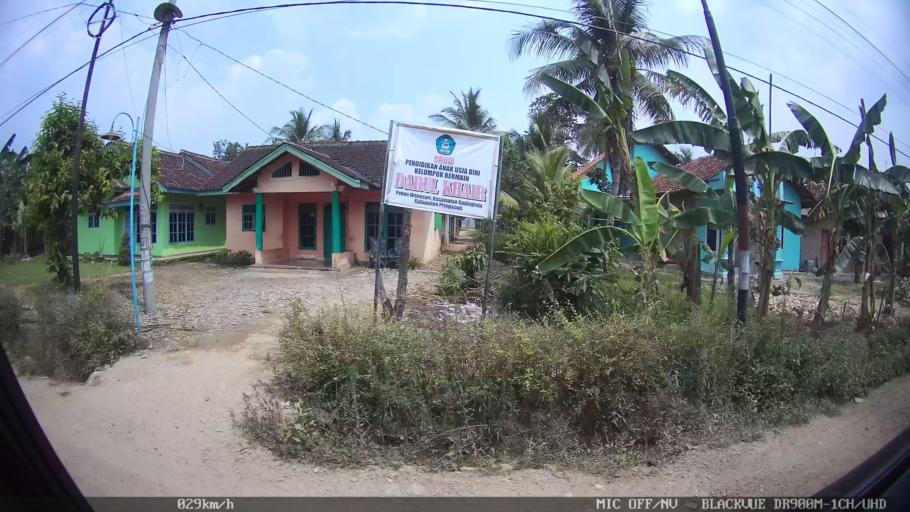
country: ID
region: Lampung
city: Gadingrejo
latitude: -5.3797
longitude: 105.0485
